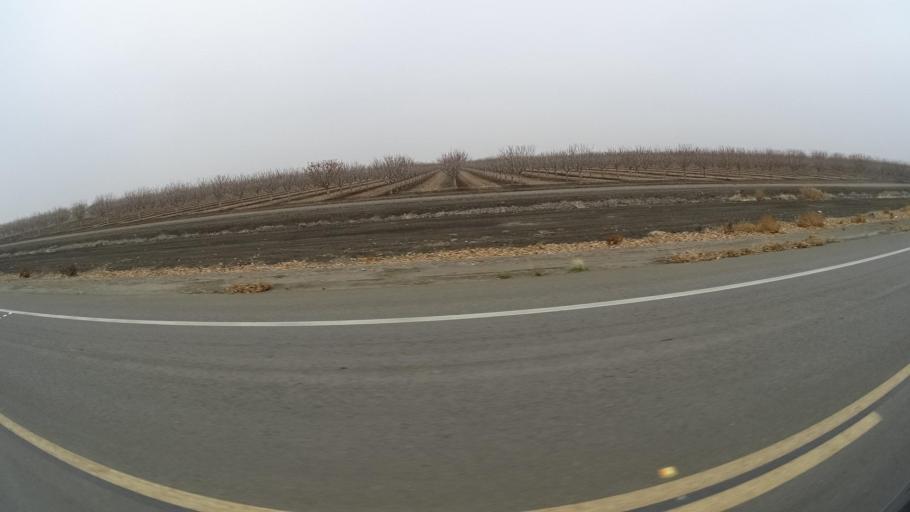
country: US
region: California
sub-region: Kern County
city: Buttonwillow
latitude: 35.3691
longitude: -119.4727
